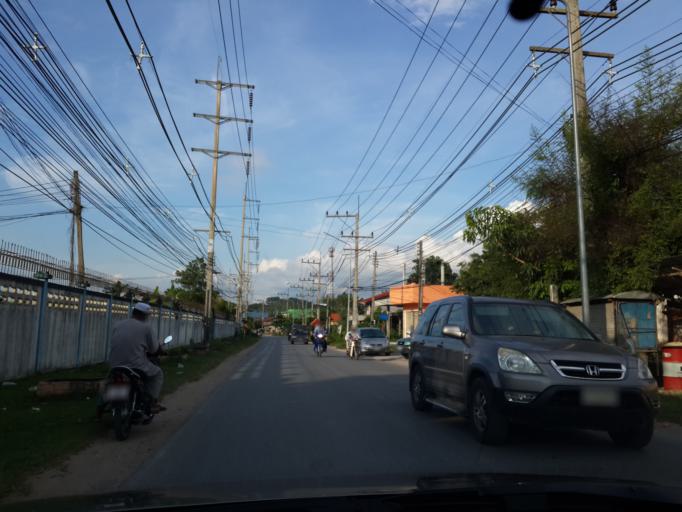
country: TH
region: Yala
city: Yala
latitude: 6.5070
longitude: 101.2696
